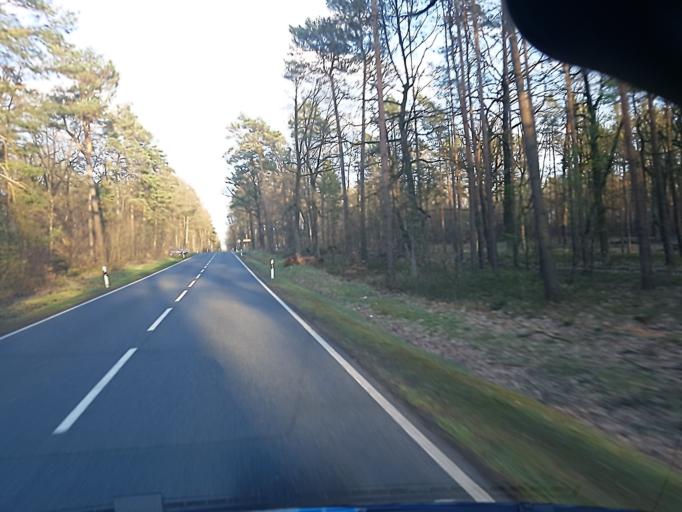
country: DE
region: Saxony
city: Doberschutz
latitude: 51.5675
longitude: 12.7628
